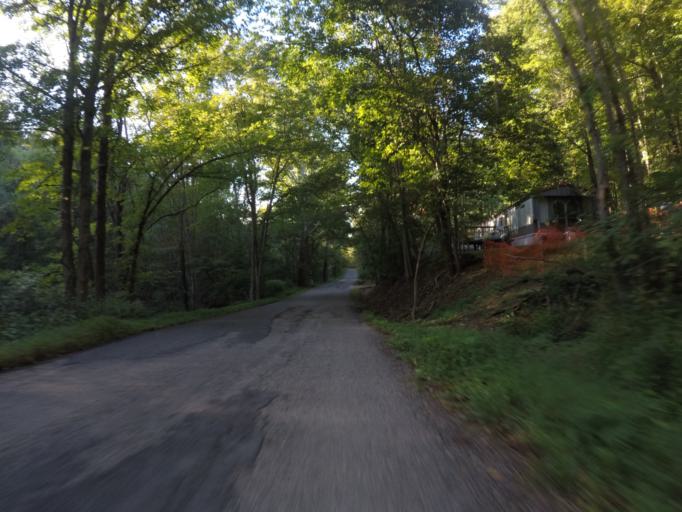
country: US
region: Kentucky
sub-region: Boyd County
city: Ashland
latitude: 38.5291
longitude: -82.5335
